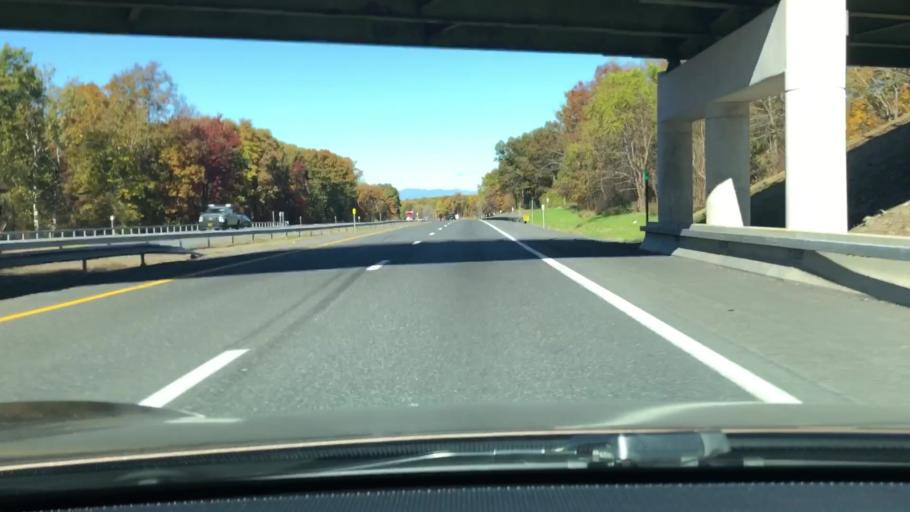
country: US
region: New York
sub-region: Ulster County
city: Clintondale
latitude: 41.6614
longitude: -74.0783
